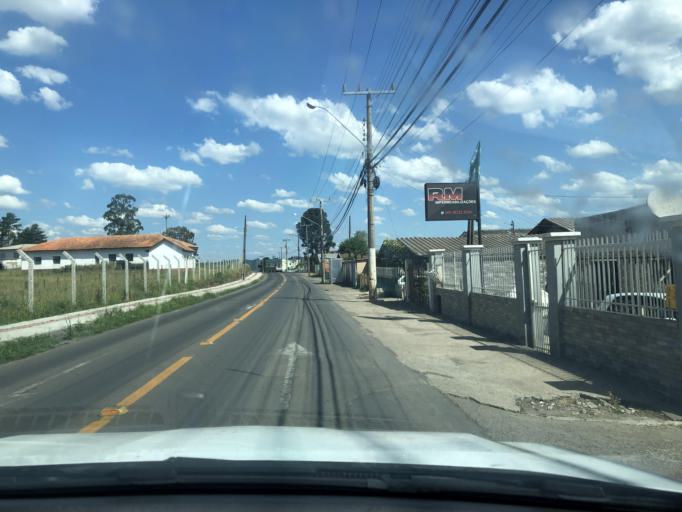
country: BR
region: Santa Catarina
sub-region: Lages
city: Lages
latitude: -27.8086
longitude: -50.3357
